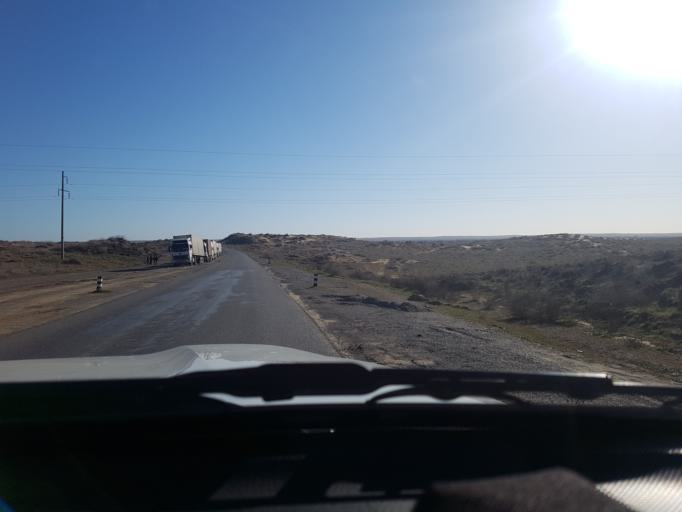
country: TM
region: Mary
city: Yoloeten
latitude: 37.0366
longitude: 62.4415
